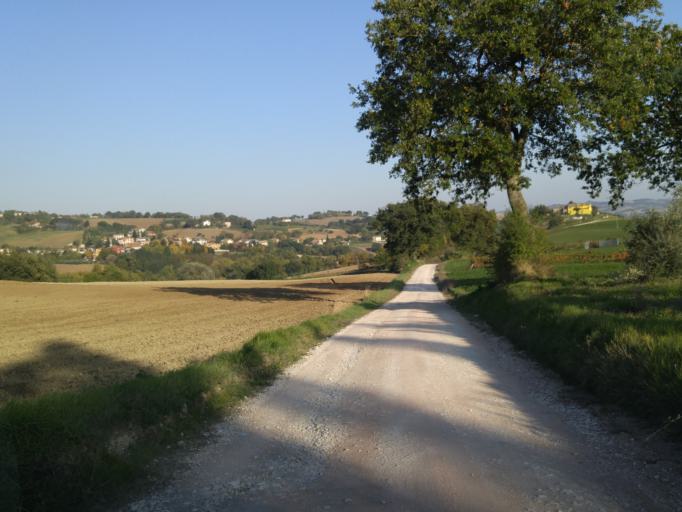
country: IT
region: The Marches
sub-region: Provincia di Pesaro e Urbino
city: Montefelcino
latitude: 43.7204
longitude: 12.8278
